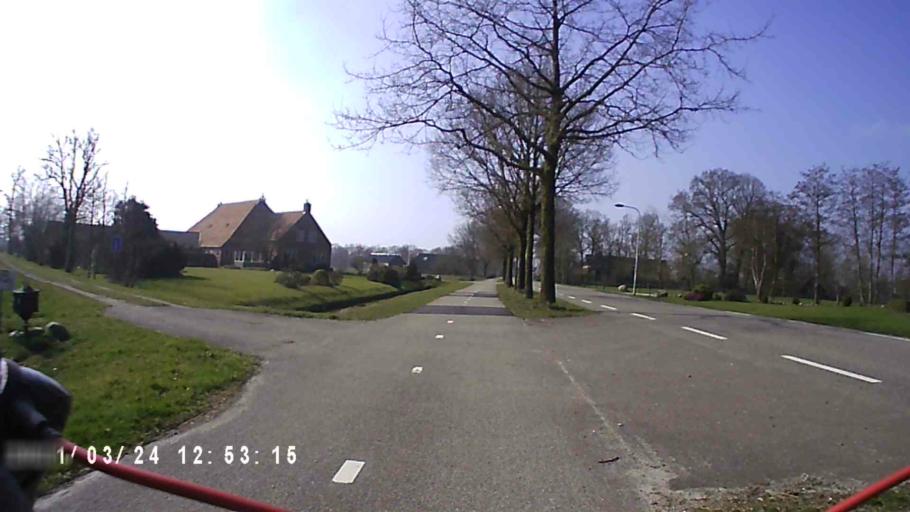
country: NL
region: Groningen
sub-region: Gemeente Leek
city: Leek
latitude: 53.1571
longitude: 6.3200
